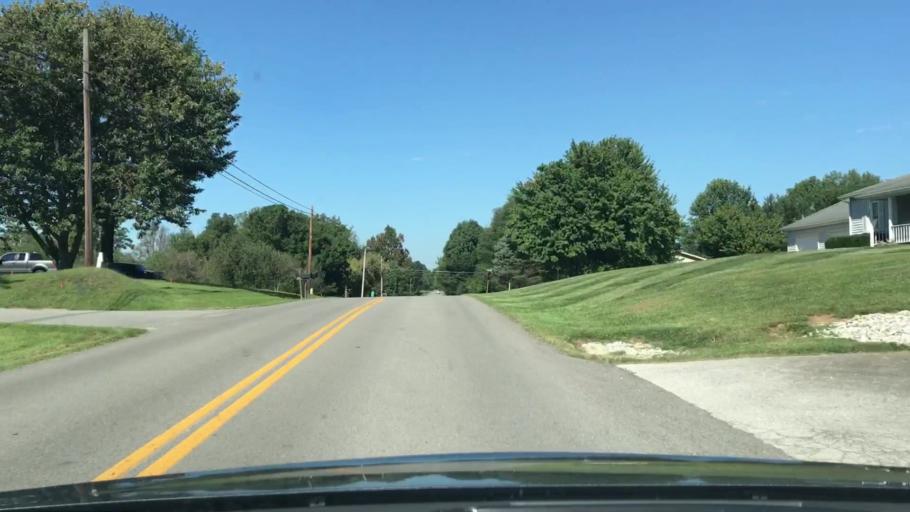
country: US
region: Kentucky
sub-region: Hardin County
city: Elizabethtown
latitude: 37.5986
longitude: -85.8760
